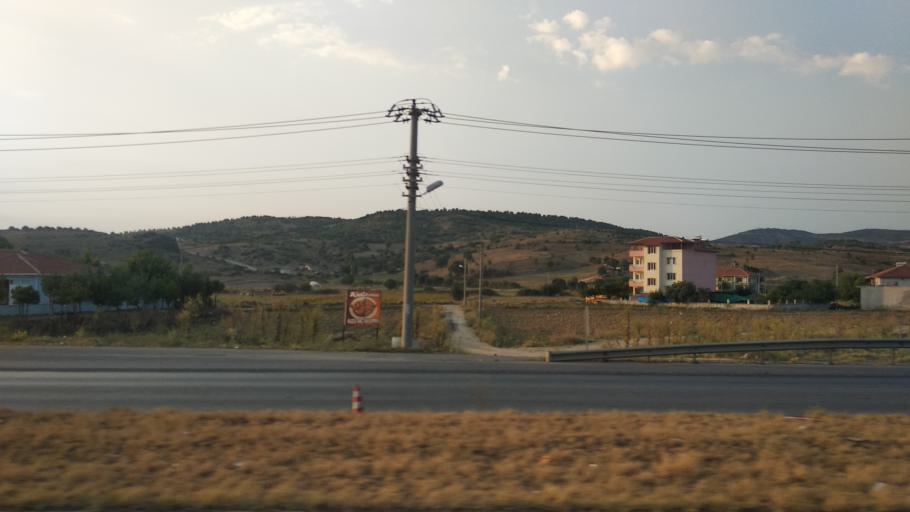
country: TR
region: Manisa
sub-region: Kula
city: Kula
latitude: 38.5441
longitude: 28.6608
